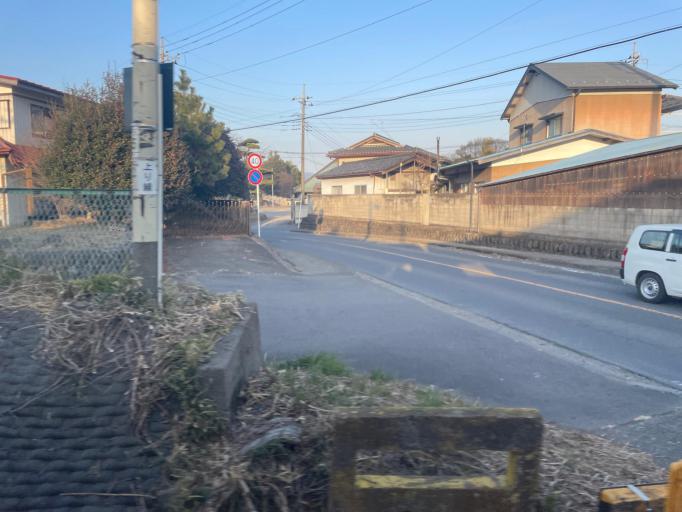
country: JP
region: Gunma
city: Kanekomachi
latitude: 36.4395
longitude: 139.0269
